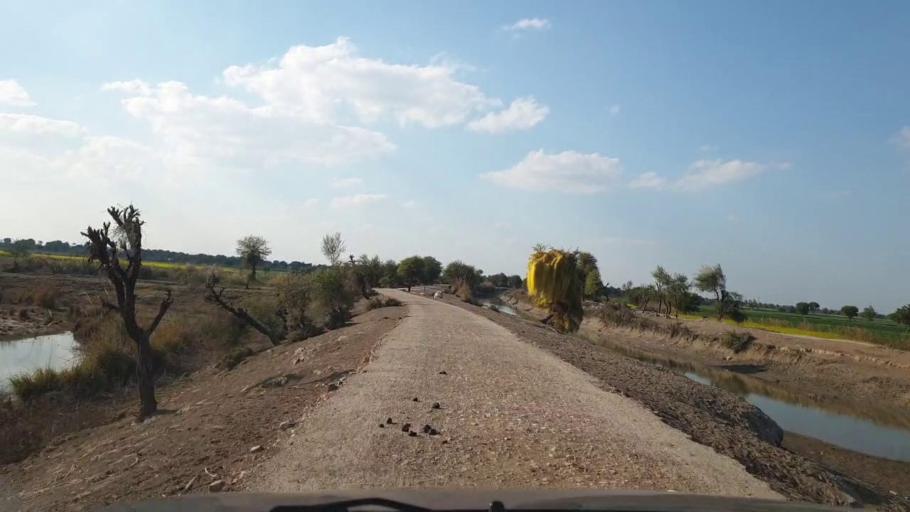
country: PK
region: Sindh
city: Sinjhoro
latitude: 25.9967
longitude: 68.7293
